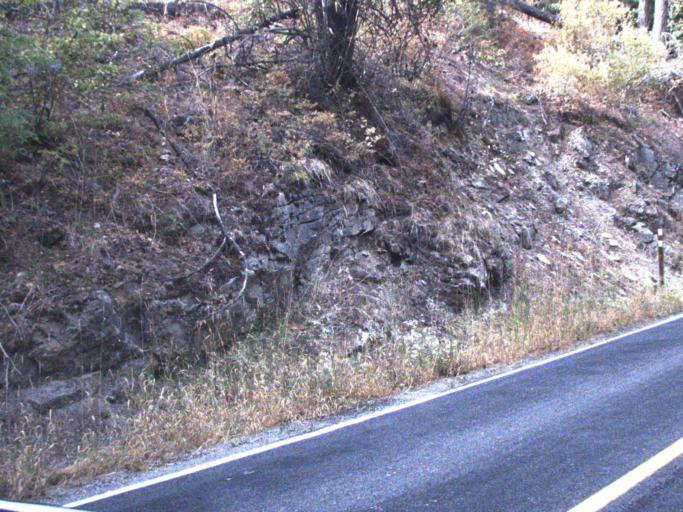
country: US
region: Washington
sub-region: Spokane County
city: Trentwood
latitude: 47.8599
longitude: -117.1624
